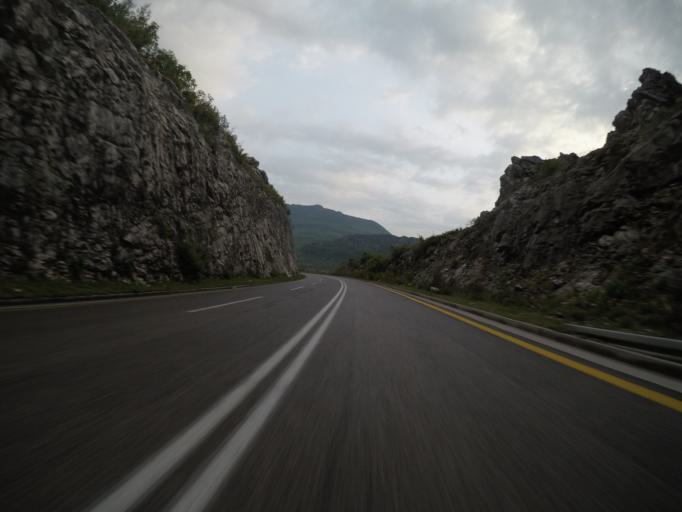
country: ME
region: Bar
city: Sutomore
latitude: 42.2194
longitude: 19.0516
